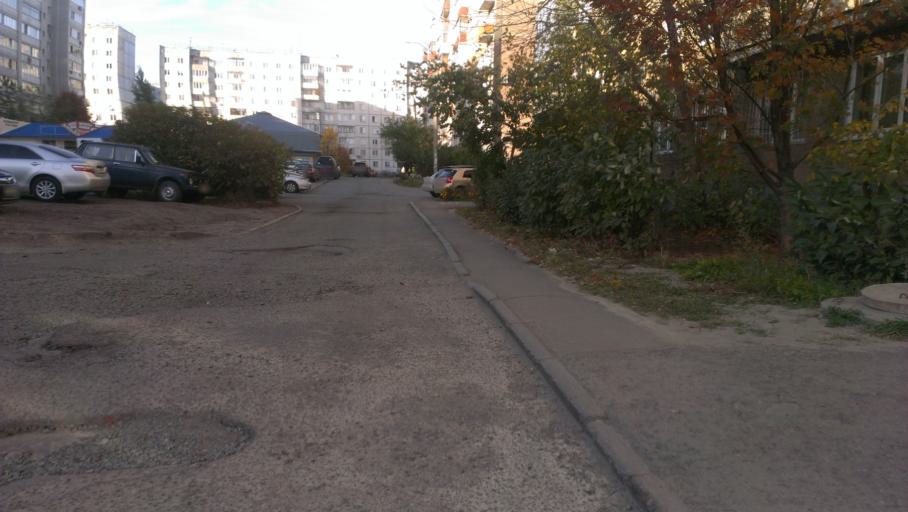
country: RU
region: Altai Krai
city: Novosilikatnyy
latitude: 53.3403
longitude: 83.6722
